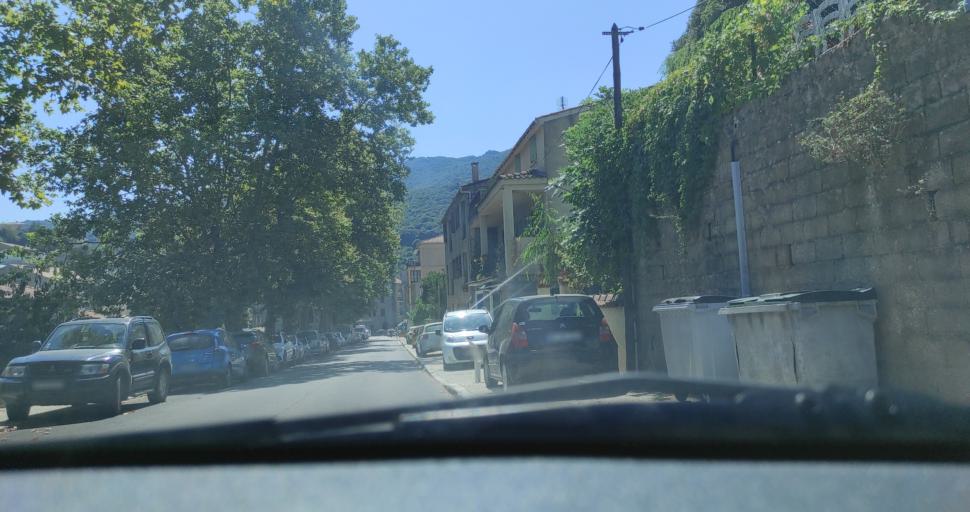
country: FR
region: Corsica
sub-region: Departement de la Corse-du-Sud
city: Sartene
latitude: 41.6187
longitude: 8.9712
